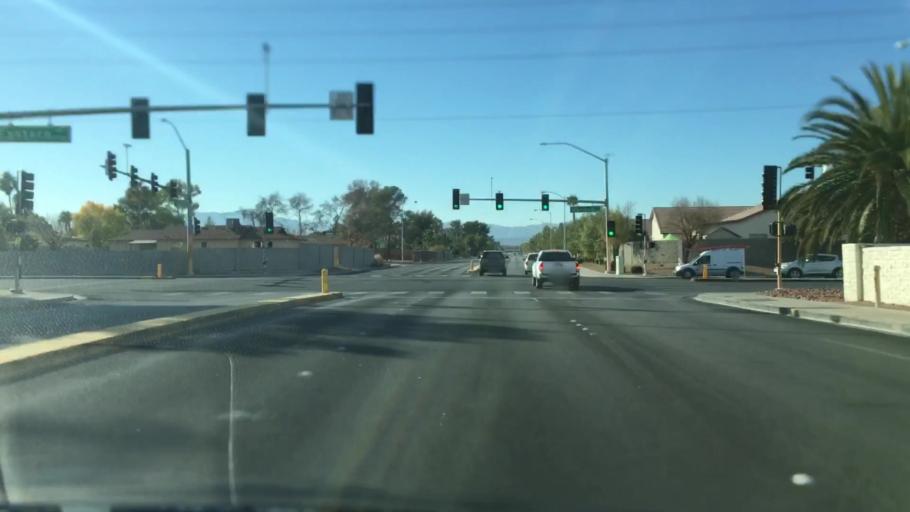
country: US
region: Nevada
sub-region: Clark County
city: Whitney
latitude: 36.0496
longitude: -115.1177
